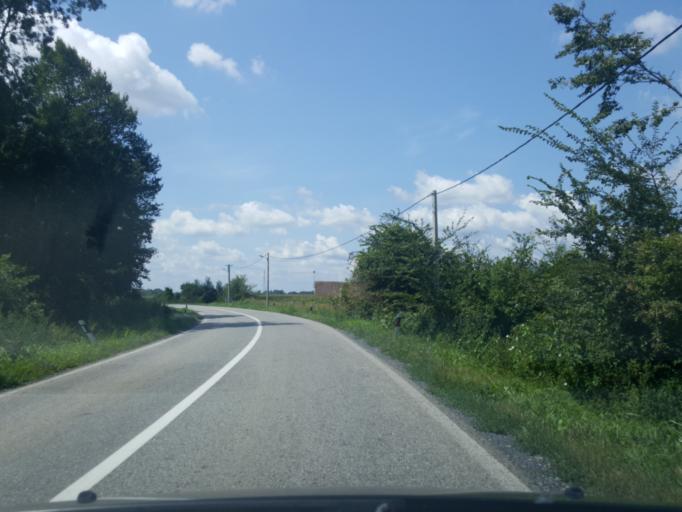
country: RS
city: Metkovic
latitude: 44.8507
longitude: 19.5278
